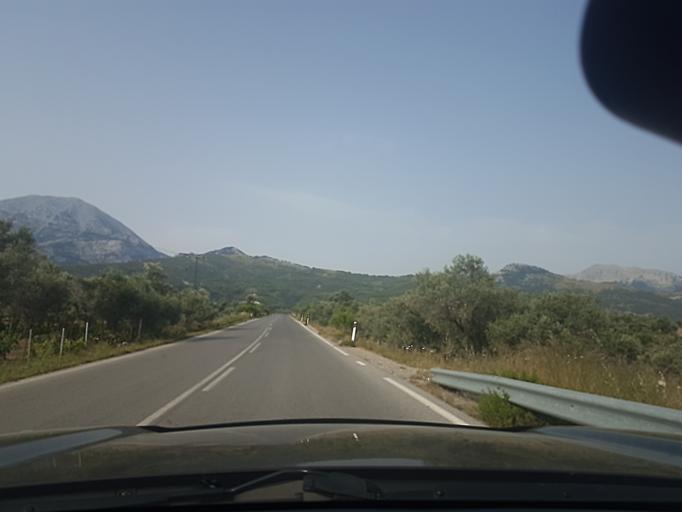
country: GR
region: Central Greece
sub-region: Nomos Evvoias
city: Yimnon
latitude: 38.5731
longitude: 23.8017
